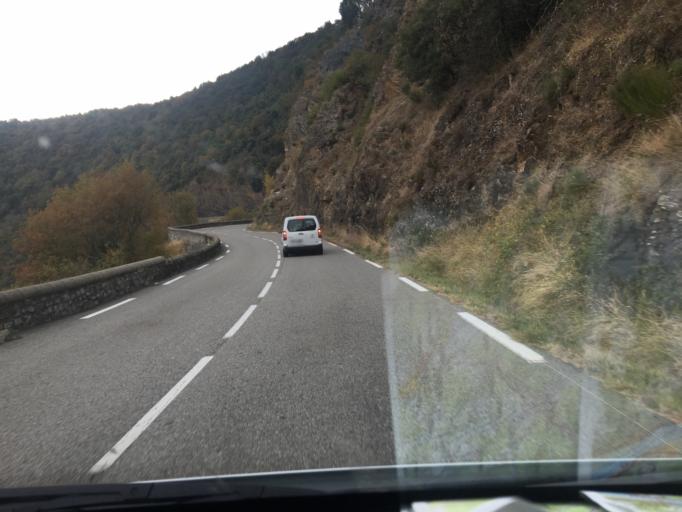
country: FR
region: Rhone-Alpes
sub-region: Departement de l'Ardeche
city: Saint-Jean-de-Muzols
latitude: 45.0655
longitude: 4.7599
